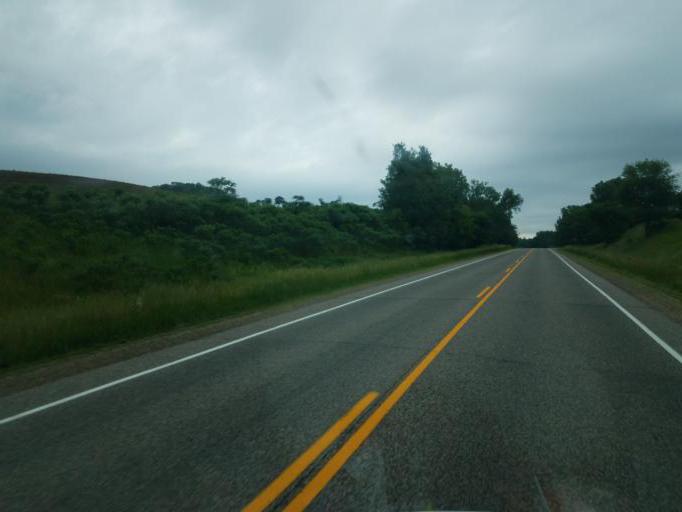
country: US
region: Wisconsin
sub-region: Juneau County
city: Elroy
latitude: 43.7767
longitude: -90.2020
